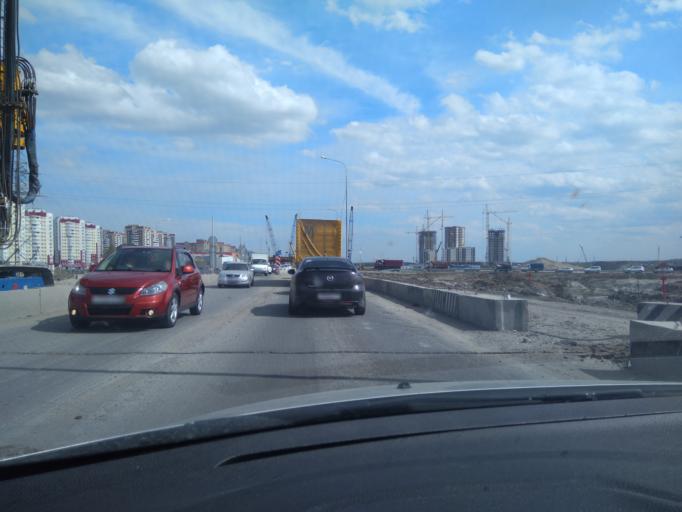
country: RU
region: Tjumen
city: Tyumen
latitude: 57.1056
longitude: 65.5598
